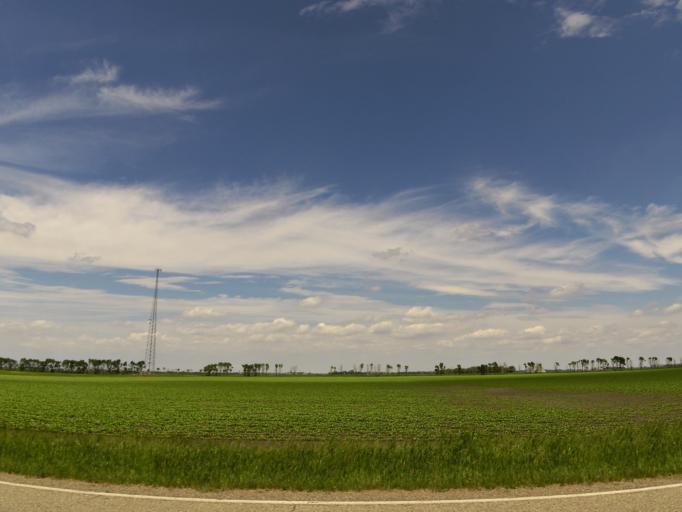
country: US
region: North Dakota
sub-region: Walsh County
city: Grafton
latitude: 48.2954
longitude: -97.2308
